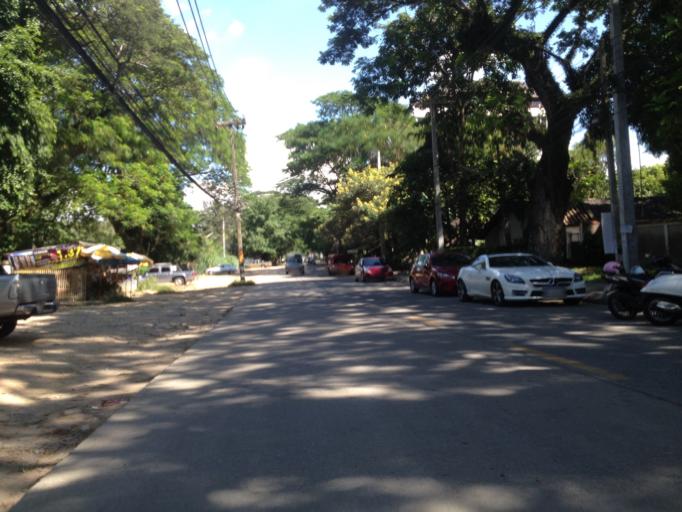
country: TH
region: Chiang Mai
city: Chiang Mai
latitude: 18.7943
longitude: 98.9498
